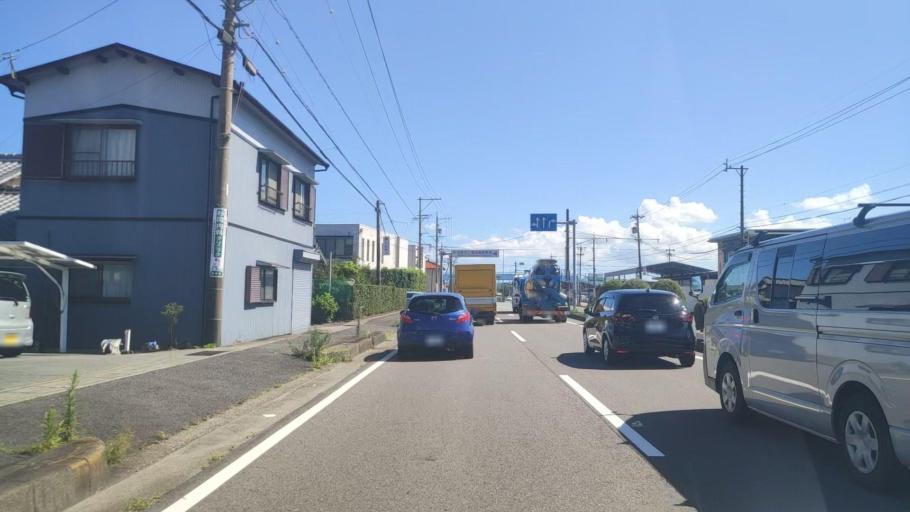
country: JP
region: Mie
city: Hisai-motomachi
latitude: 34.6276
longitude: 136.5165
